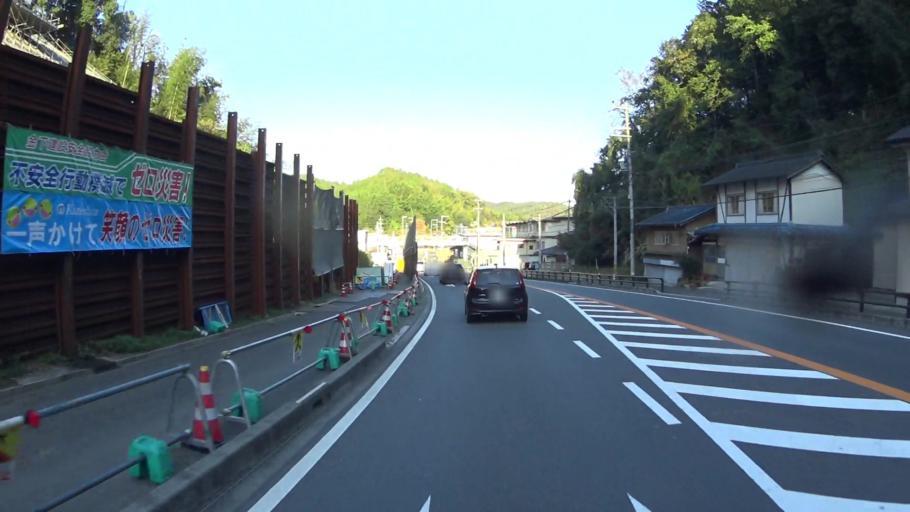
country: JP
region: Kyoto
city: Ayabe
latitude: 35.1877
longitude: 135.3220
